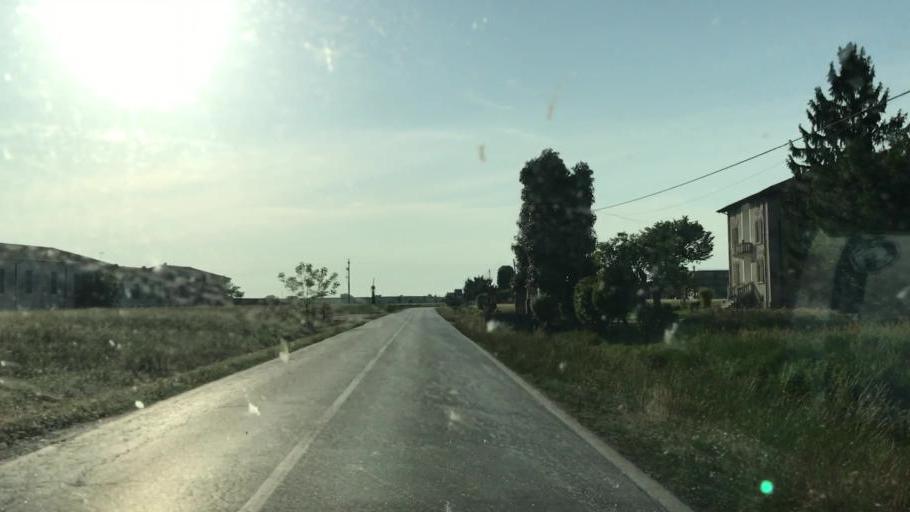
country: IT
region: Lombardy
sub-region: Provincia di Mantova
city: Casaloldo
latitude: 45.2454
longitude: 10.4980
